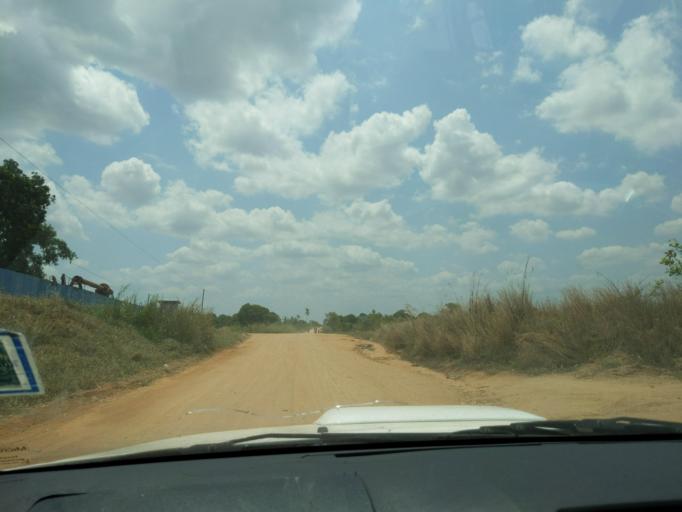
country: MZ
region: Zambezia
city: Quelimane
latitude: -17.2576
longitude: 37.0681
